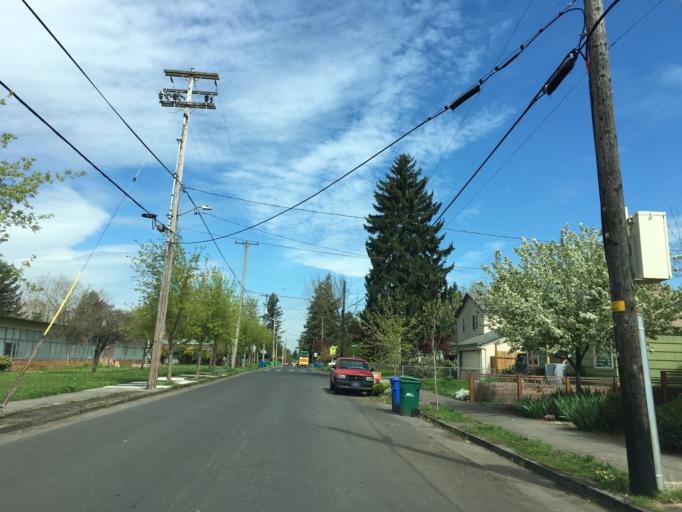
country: US
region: Oregon
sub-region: Multnomah County
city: Lents
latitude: 45.5287
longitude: -122.5866
